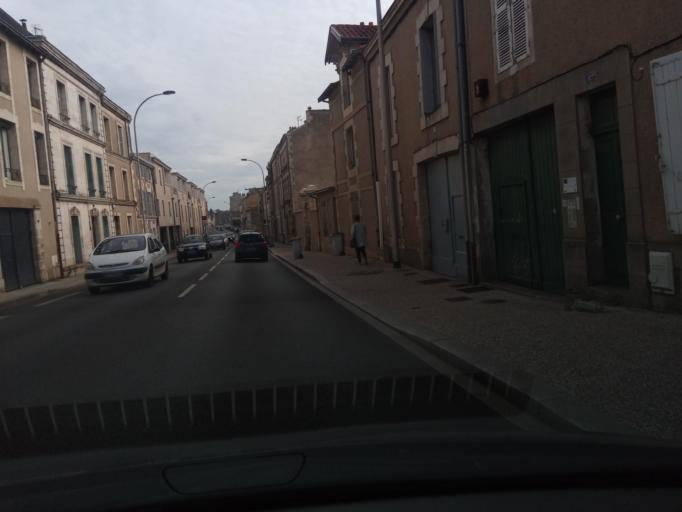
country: FR
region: Poitou-Charentes
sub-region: Departement de la Vienne
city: Poitiers
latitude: 46.5700
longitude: 0.3235
